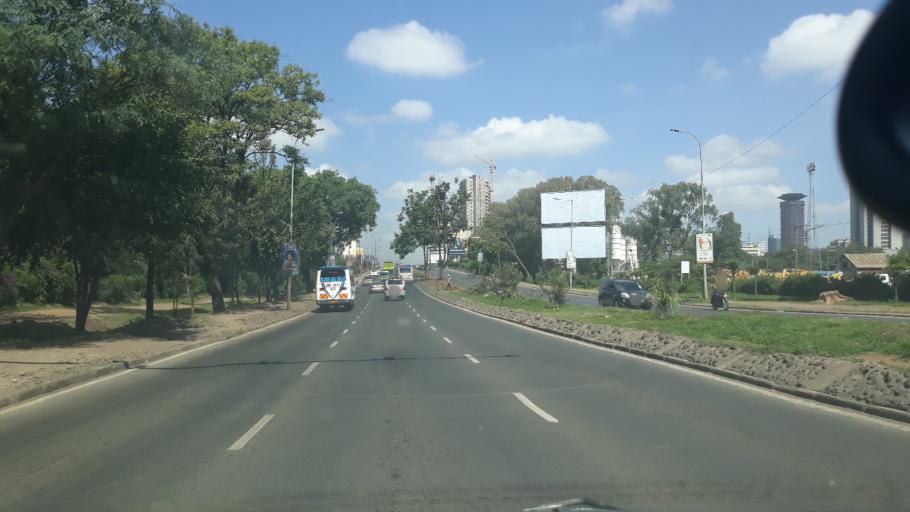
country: KE
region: Nairobi Area
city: Nairobi
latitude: -1.2977
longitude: 36.8233
